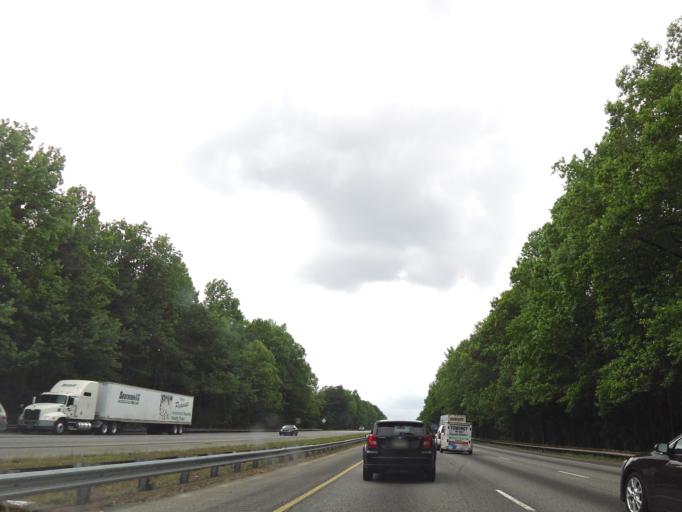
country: US
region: Georgia
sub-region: Douglas County
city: Lithia Springs
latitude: 33.7599
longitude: -84.6836
